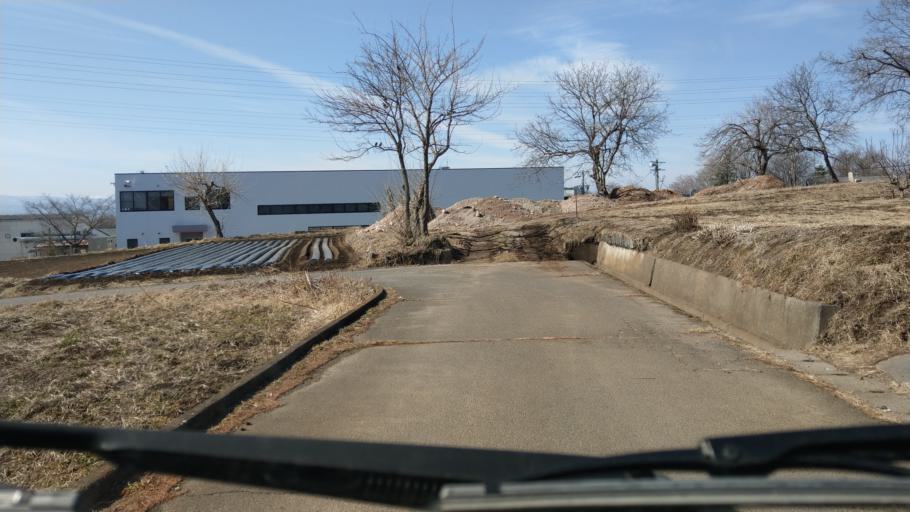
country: JP
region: Nagano
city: Komoro
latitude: 36.3180
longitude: 138.4485
